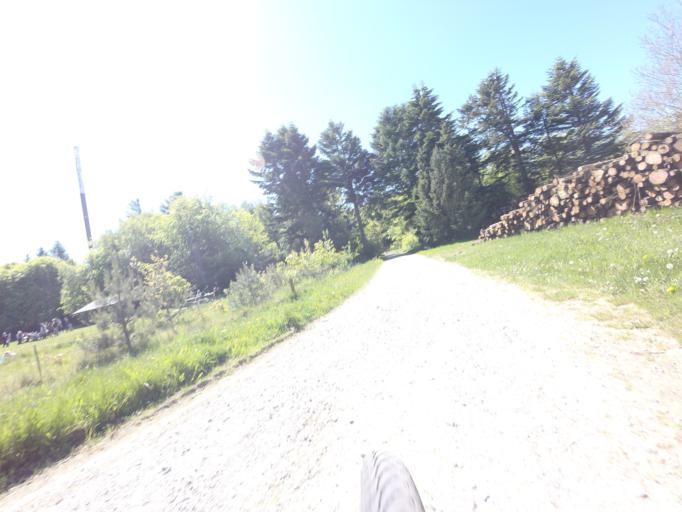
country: DK
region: North Denmark
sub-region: Jammerbugt Kommune
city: Pandrup
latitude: 57.2474
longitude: 9.6003
